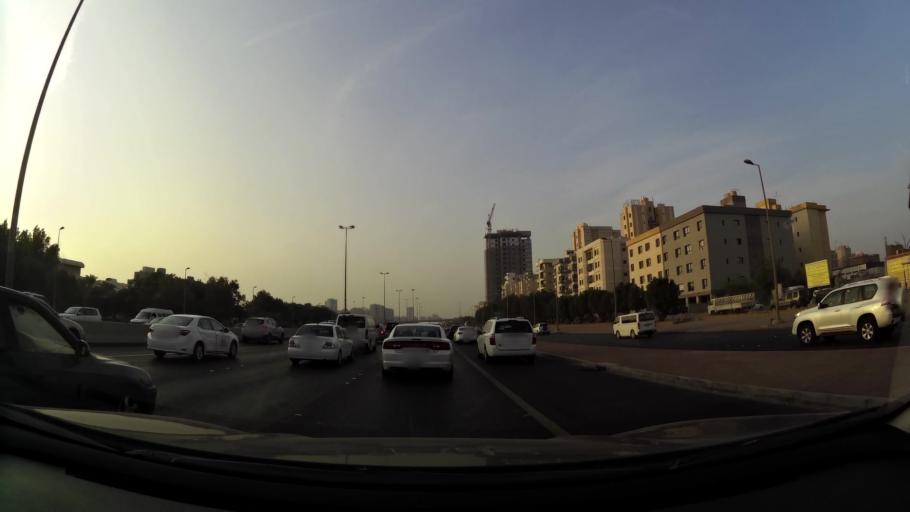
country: KW
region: Muhafazat Hawalli
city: Hawalli
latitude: 29.3257
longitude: 48.0439
